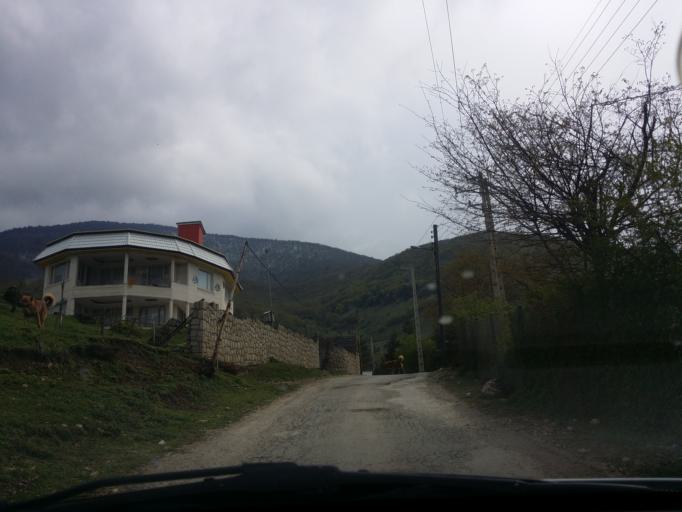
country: IR
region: Mazandaran
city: `Abbasabad
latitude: 36.4886
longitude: 51.1521
